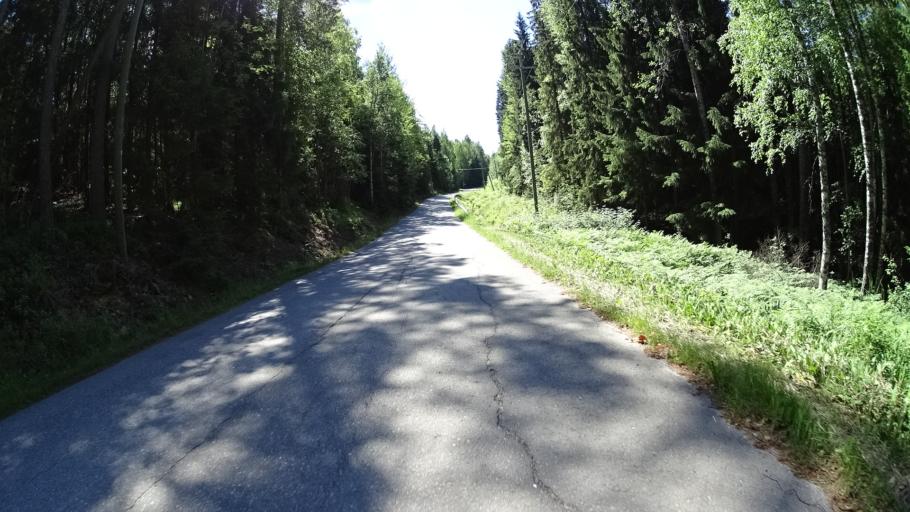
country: FI
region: Uusimaa
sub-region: Helsinki
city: Vihti
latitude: 60.3074
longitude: 24.4394
